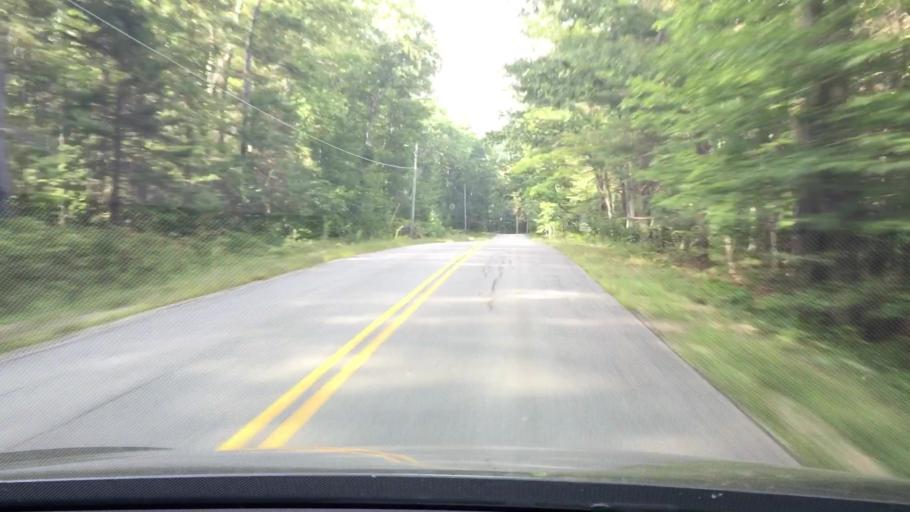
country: US
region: Maine
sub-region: Hancock County
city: Orland
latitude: 44.5283
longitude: -68.7636
